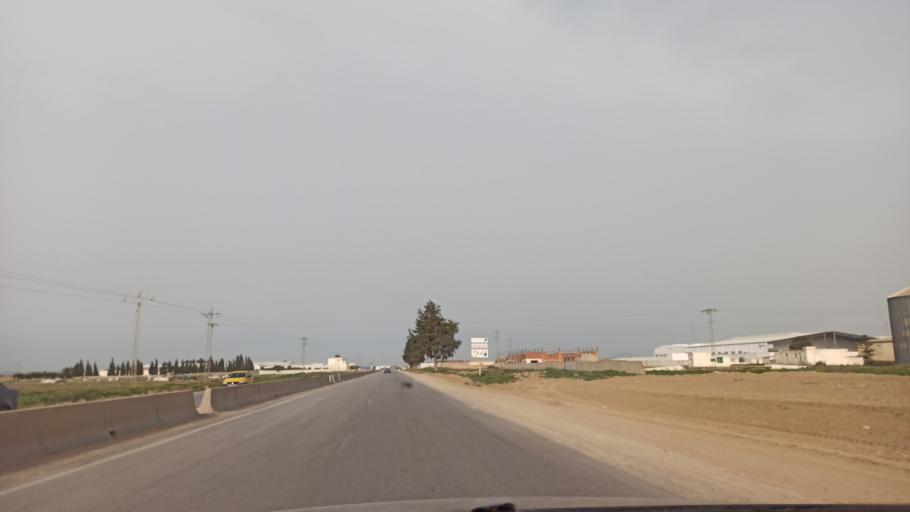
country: TN
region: Tunis
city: La Mohammedia
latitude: 36.5800
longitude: 10.0946
